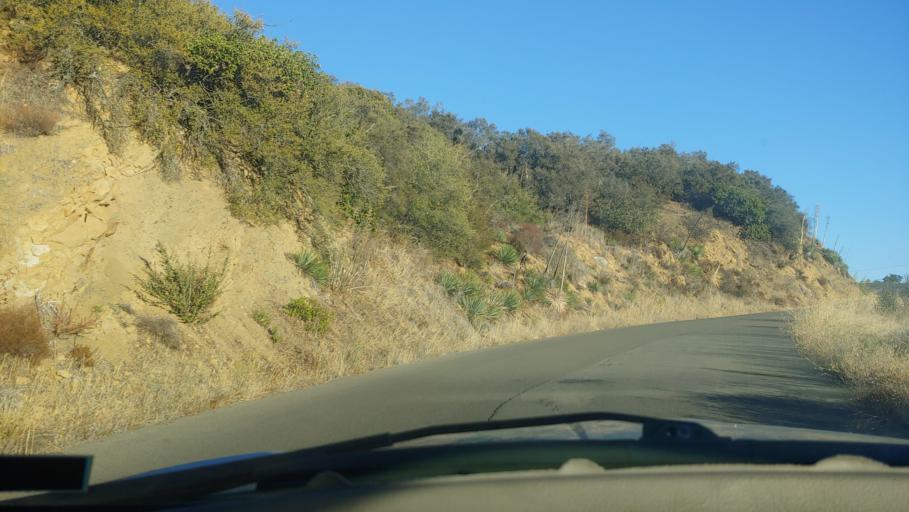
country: US
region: California
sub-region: Santa Barbara County
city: Goleta
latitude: 34.5192
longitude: -119.7899
